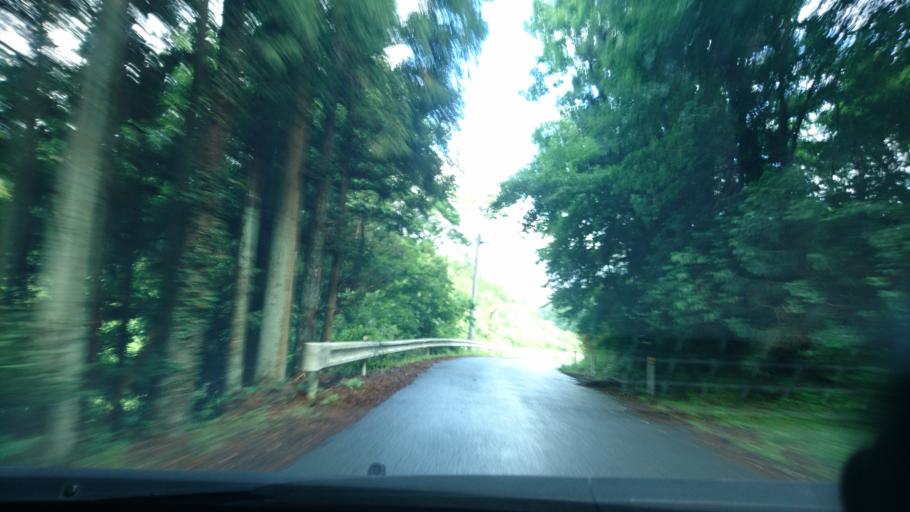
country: JP
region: Iwate
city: Ichinoseki
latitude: 38.8669
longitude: 141.2845
